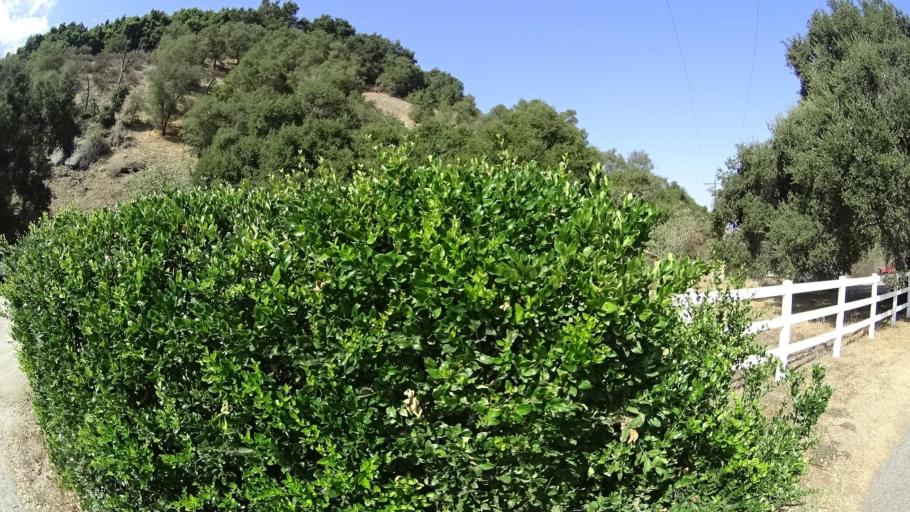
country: US
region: California
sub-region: San Diego County
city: Valley Center
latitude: 33.3068
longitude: -117.0013
